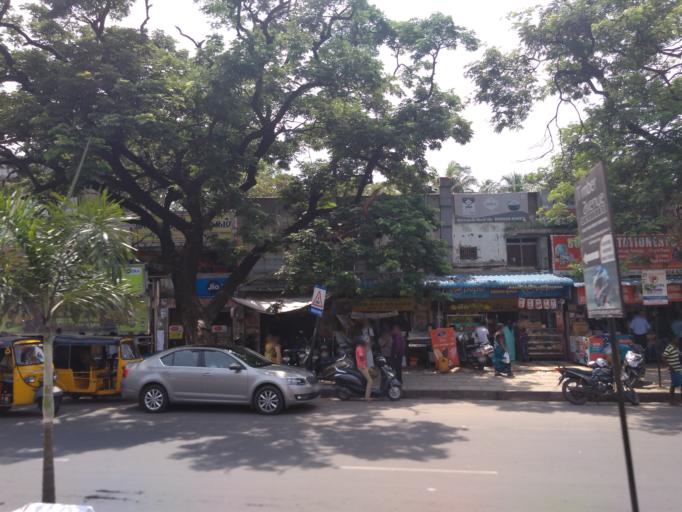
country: IN
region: Tamil Nadu
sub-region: Chennai
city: Gandhi Nagar
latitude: 12.9992
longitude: 80.2561
